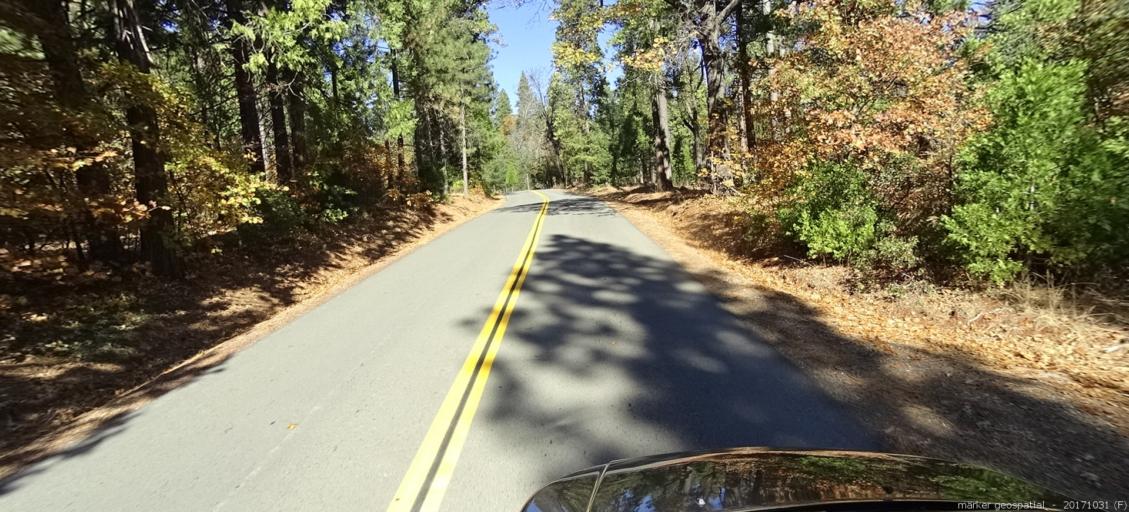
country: US
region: California
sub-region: Shasta County
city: Shingletown
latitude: 40.4802
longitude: -121.8762
